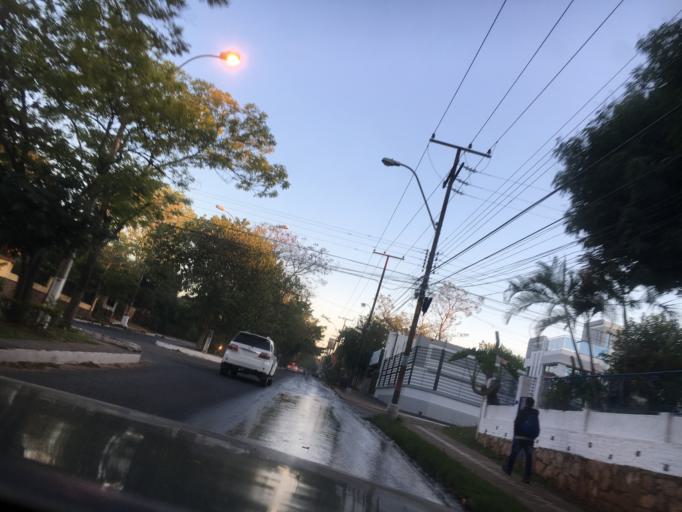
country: PY
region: Central
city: Lambare
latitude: -25.3385
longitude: -57.6058
